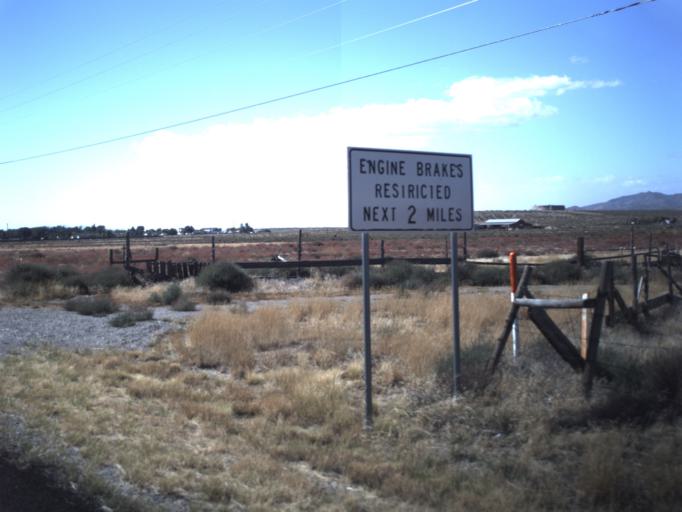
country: US
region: Utah
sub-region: Beaver County
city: Milford
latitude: 38.4123
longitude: -113.0099
